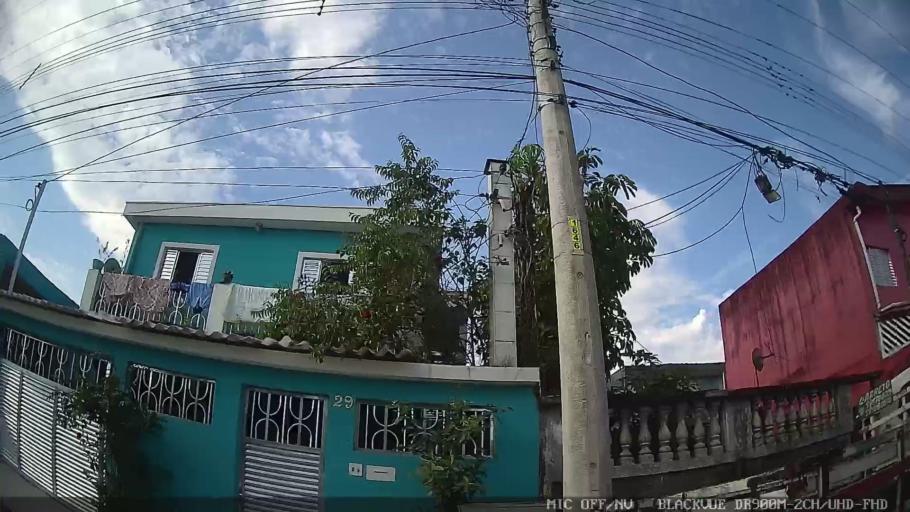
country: BR
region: Sao Paulo
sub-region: Guaruja
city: Guaruja
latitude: -23.9645
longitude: -46.2564
